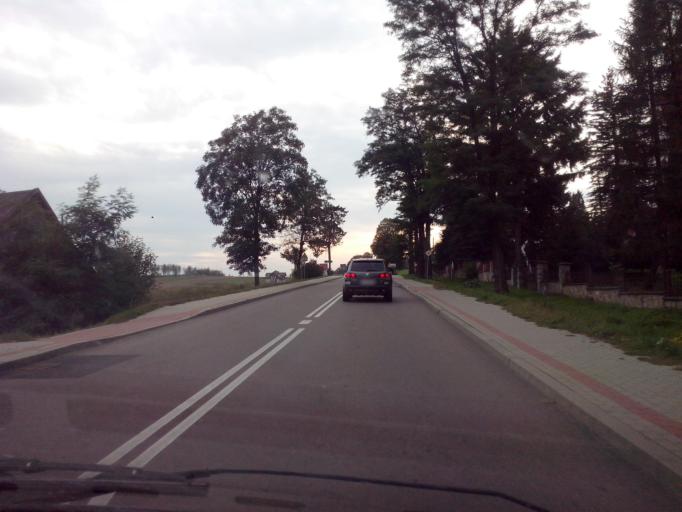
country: PL
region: Subcarpathian Voivodeship
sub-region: Powiat przemyski
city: Przedmiescie Dubieckie
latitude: 49.8260
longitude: 22.3297
